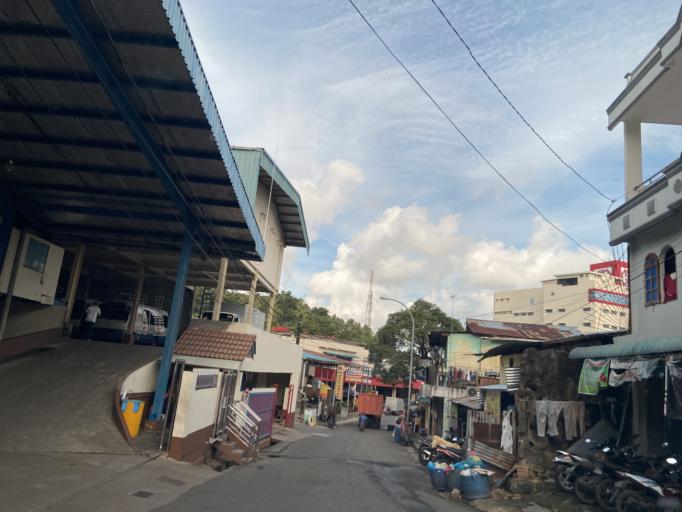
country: SG
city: Singapore
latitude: 1.1402
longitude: 104.0198
